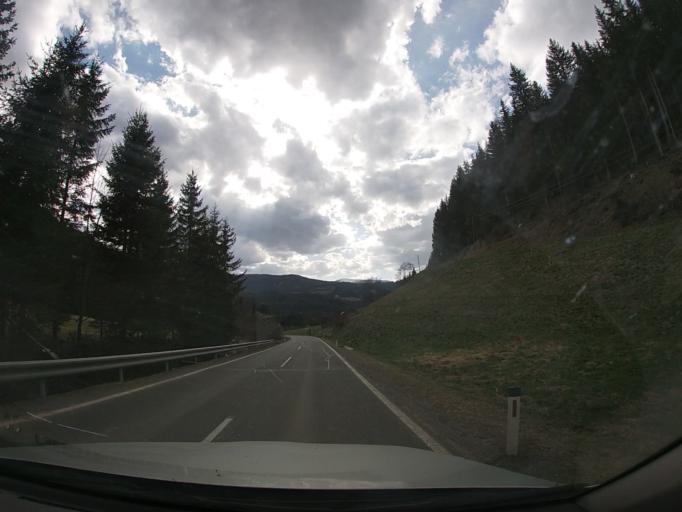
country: AT
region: Styria
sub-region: Politischer Bezirk Murau
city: Triebendorf
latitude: 47.0586
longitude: 14.2377
